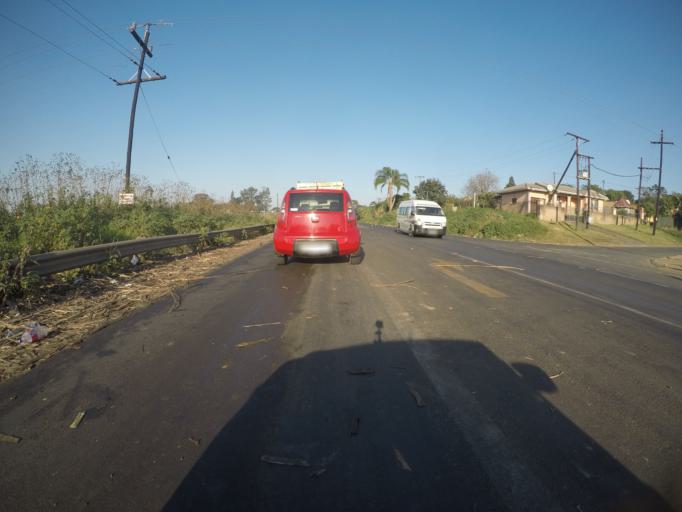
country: ZA
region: KwaZulu-Natal
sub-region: iLembe District Municipality
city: Stanger
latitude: -29.4119
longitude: 31.2445
